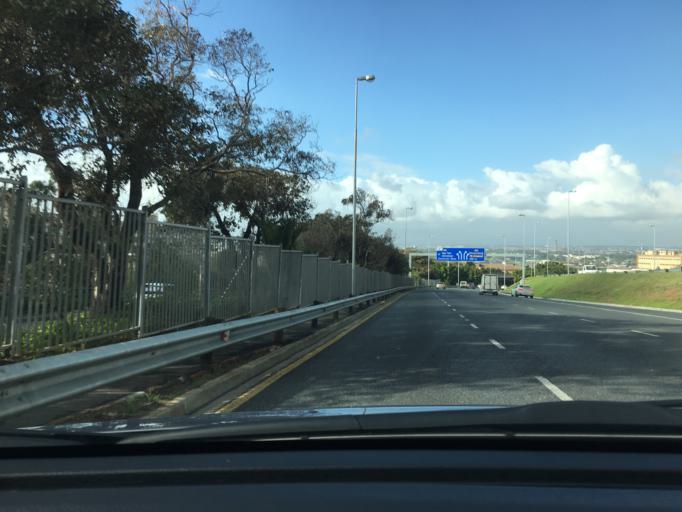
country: ZA
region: Western Cape
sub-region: City of Cape Town
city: Rosebank
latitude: -33.9432
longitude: 18.4610
